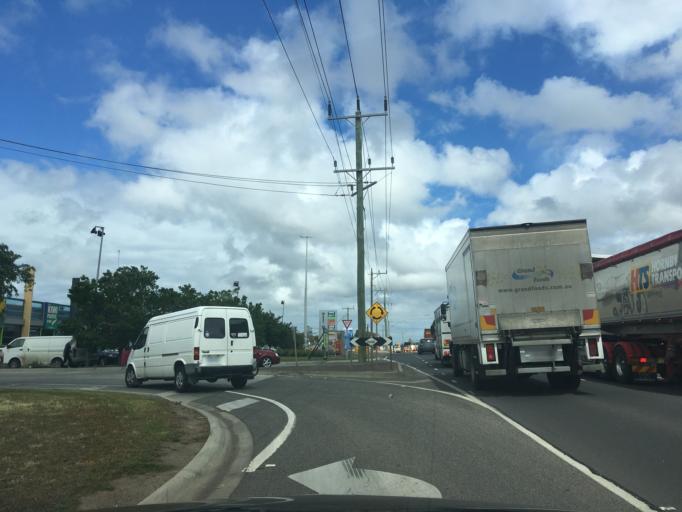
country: AU
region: Victoria
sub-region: Wyndham
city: Truganina
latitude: -37.8259
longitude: 144.7859
